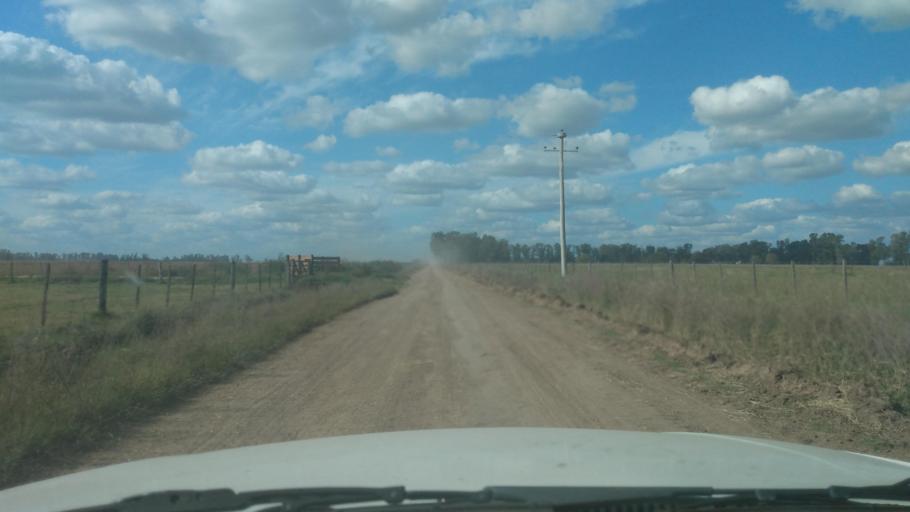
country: AR
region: Buenos Aires
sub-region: Partido de Navarro
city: Navarro
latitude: -35.0342
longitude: -59.5038
